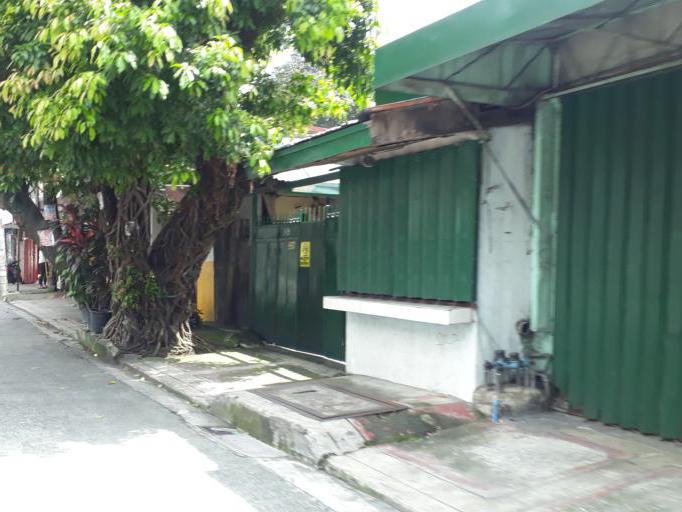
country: PH
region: Calabarzon
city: Bagong Pagasa
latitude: 14.6618
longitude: 121.0348
